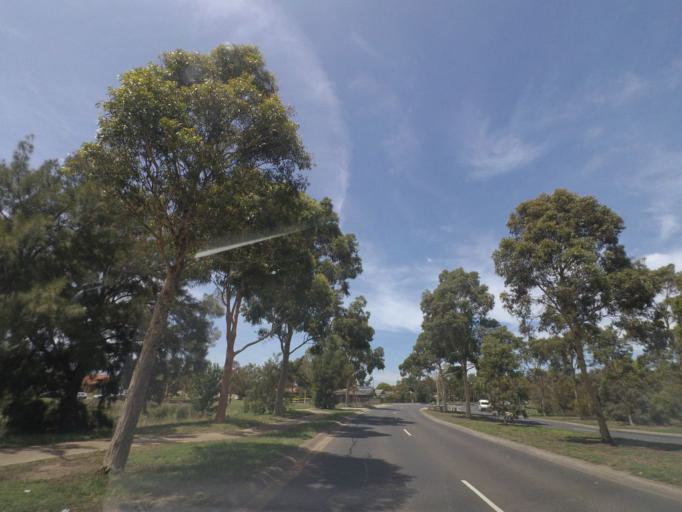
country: AU
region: Victoria
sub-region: Hume
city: Roxburgh Park
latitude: -37.6351
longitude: 144.9222
